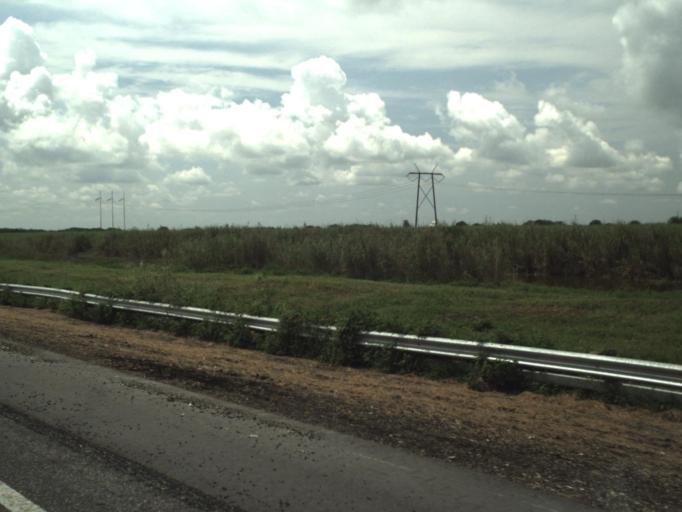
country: US
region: Florida
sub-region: Palm Beach County
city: Loxahatchee Groves
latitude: 26.7181
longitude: -80.4301
